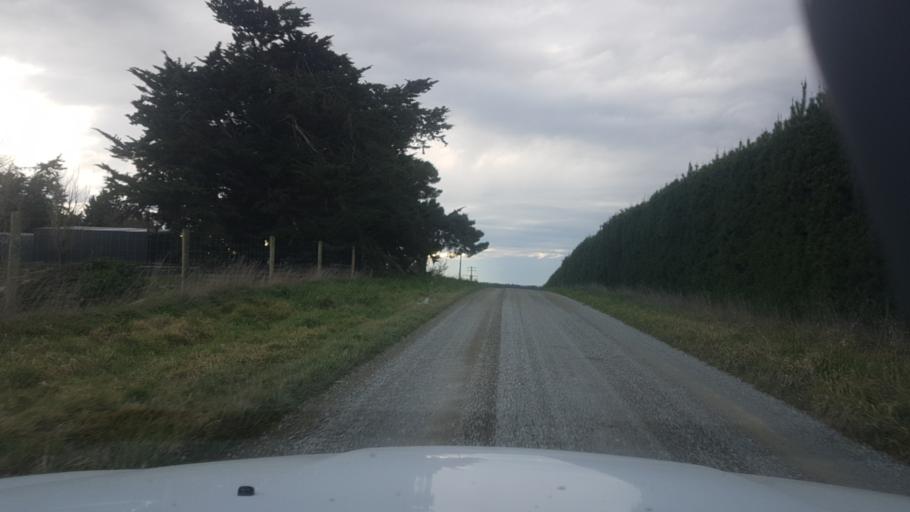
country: NZ
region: Canterbury
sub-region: Timaru District
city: Pleasant Point
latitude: -44.3381
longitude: 171.1474
